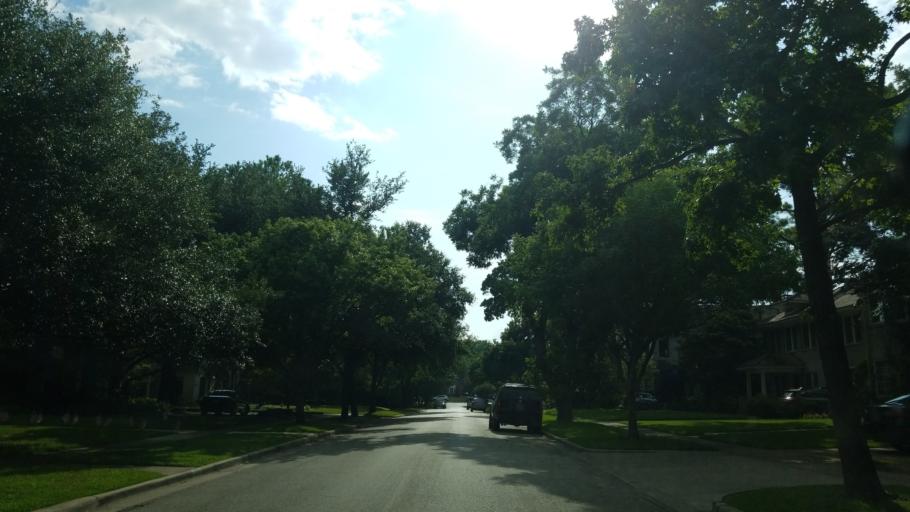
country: US
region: Texas
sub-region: Dallas County
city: University Park
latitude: 32.8430
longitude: -96.8024
